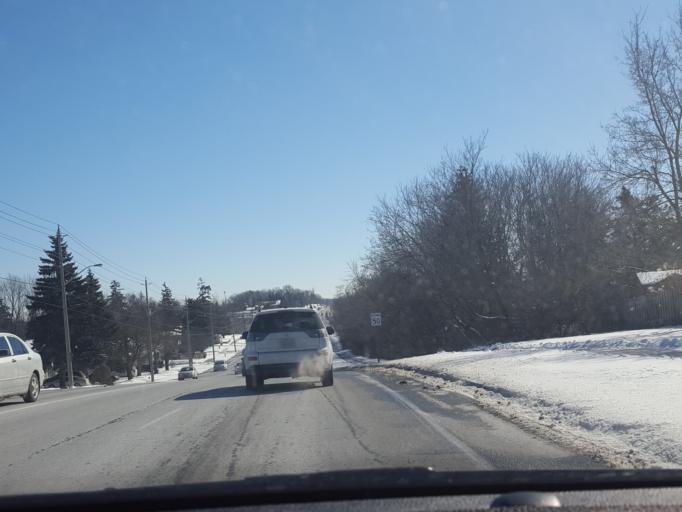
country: CA
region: Ontario
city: Kitchener
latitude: 43.4234
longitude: -80.5191
